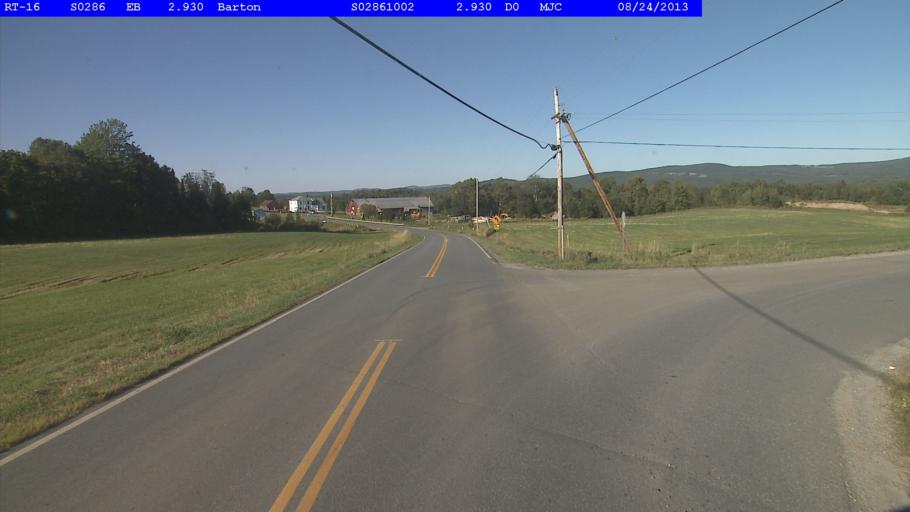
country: US
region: Vermont
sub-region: Orleans County
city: Newport
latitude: 44.7649
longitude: -72.1287
